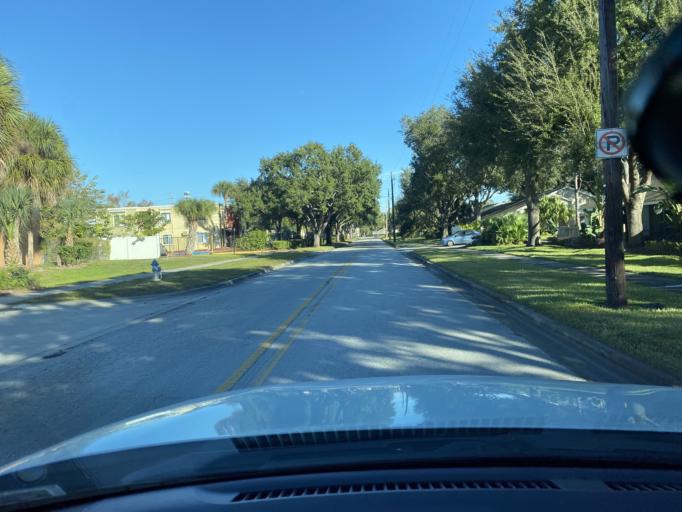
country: US
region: Florida
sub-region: Orange County
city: Azalea Park
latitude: 28.5198
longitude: -81.3062
